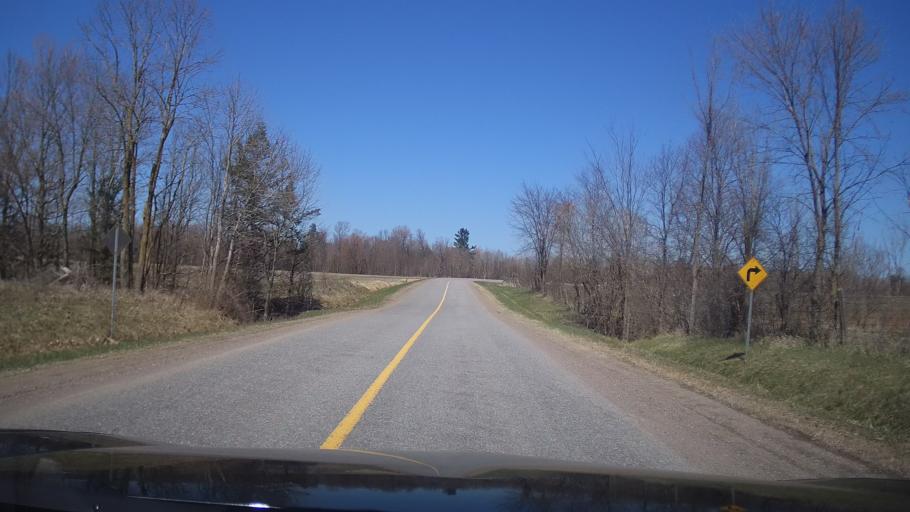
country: CA
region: Quebec
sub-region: Outaouais
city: Shawville
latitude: 45.5369
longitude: -76.3927
